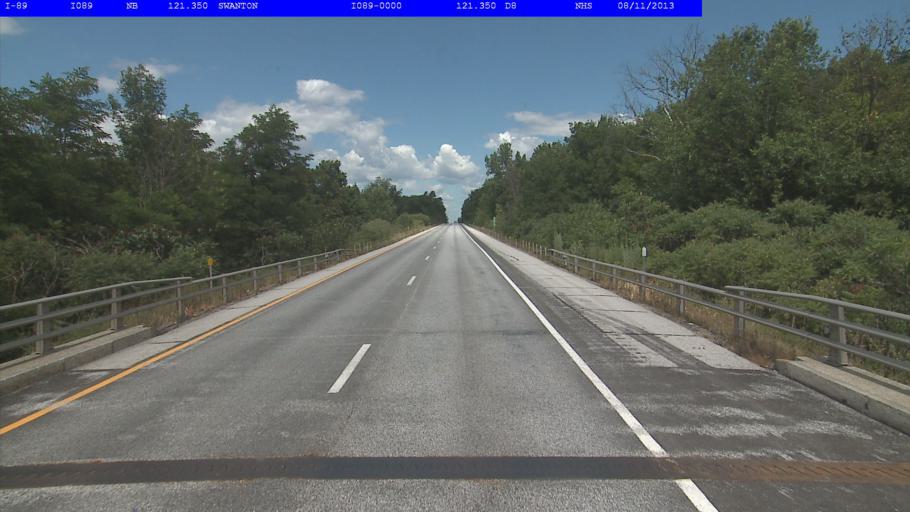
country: US
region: Vermont
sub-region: Franklin County
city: Swanton
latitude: 44.8957
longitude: -73.0902
